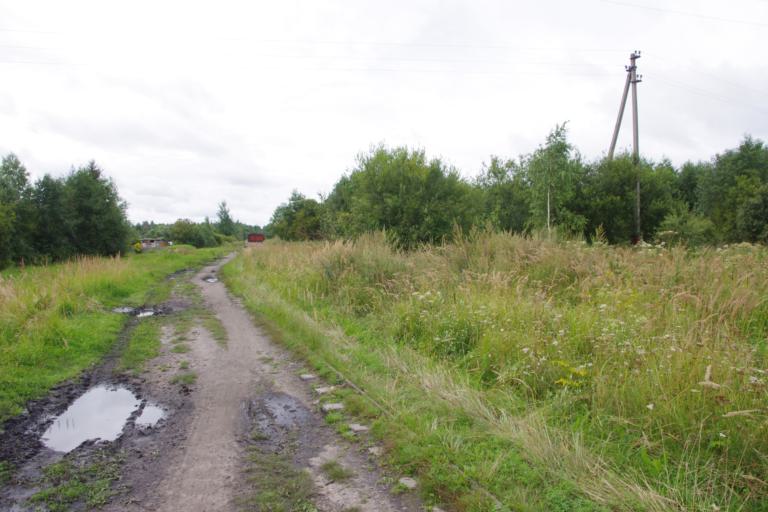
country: BY
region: Vitebsk
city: Chashniki
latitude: 55.3415
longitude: 29.3092
